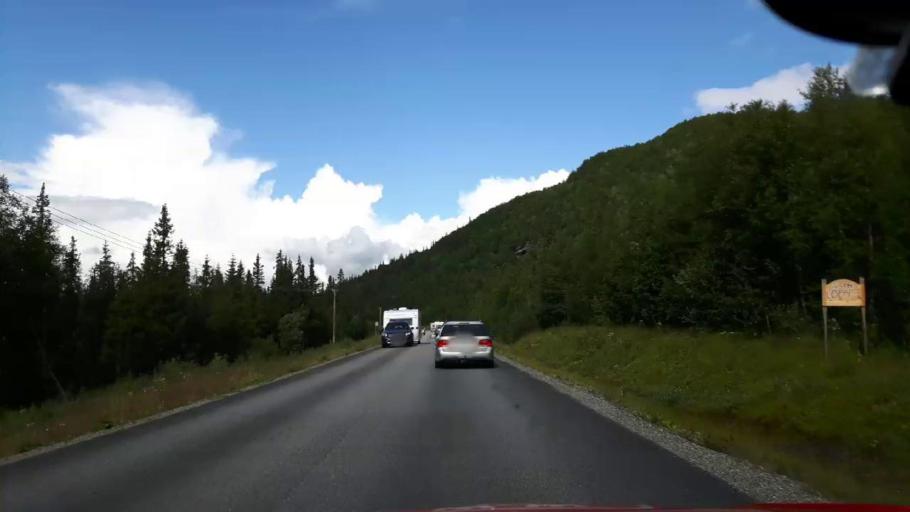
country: SE
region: Vaesterbotten
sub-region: Vilhelmina Kommun
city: Sjoberg
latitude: 65.0357
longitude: 15.1351
